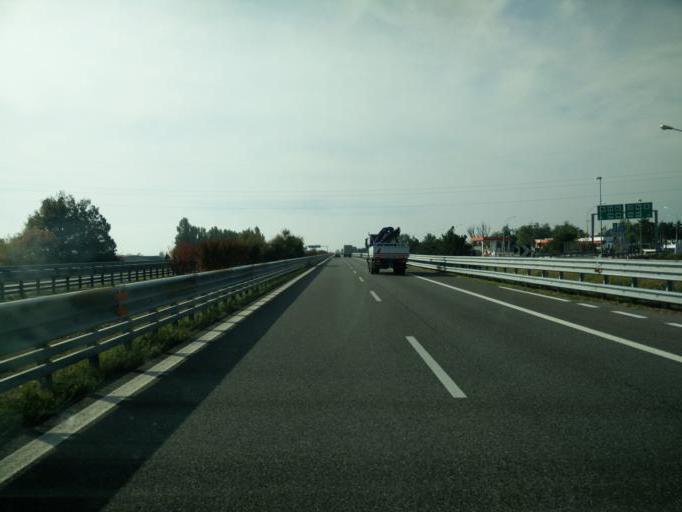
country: IT
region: Lombardy
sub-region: Provincia di Cremona
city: San Felice
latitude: 45.1415
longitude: 10.0713
